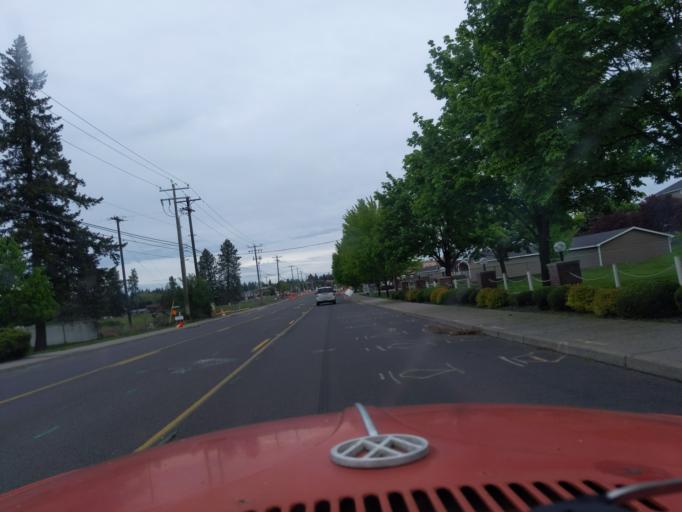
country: US
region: Washington
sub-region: Spokane County
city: Spokane
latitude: 47.6072
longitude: -117.3683
